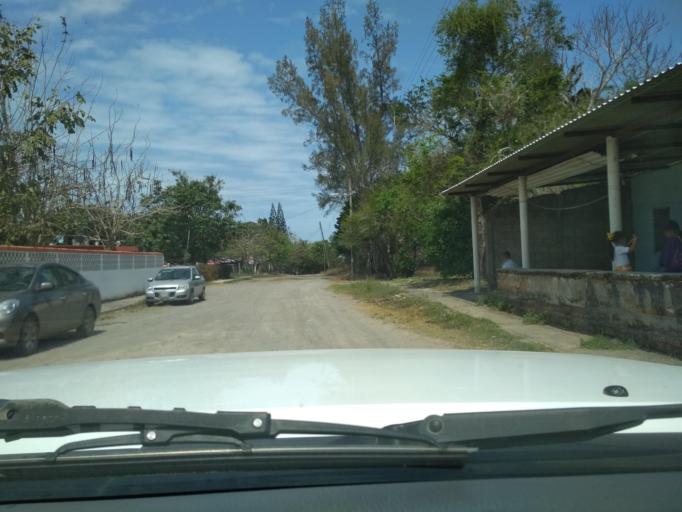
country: MX
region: Veracruz
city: Anton Lizardo
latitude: 19.0069
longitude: -95.9891
